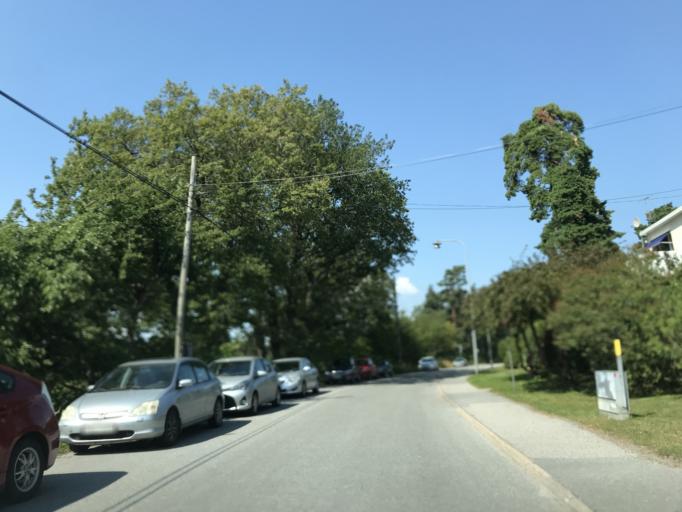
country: SE
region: Stockholm
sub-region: Stockholms Kommun
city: Bromma
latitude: 59.3323
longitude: 17.9588
